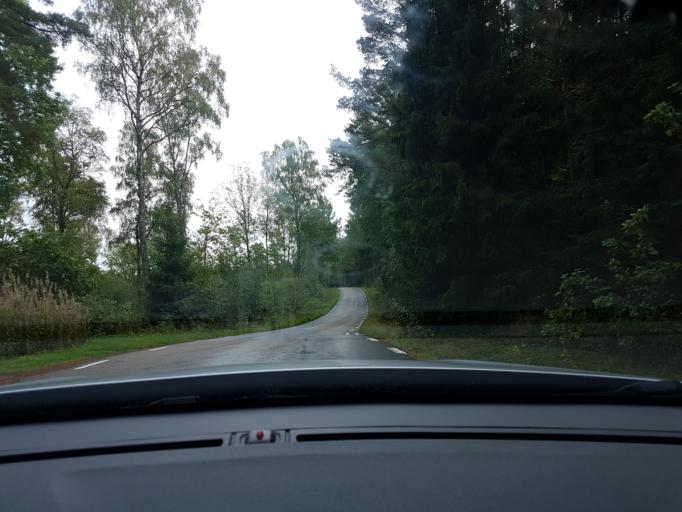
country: SE
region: Vaestra Goetaland
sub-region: Ale Kommun
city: Alvangen
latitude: 57.9019
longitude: 12.1820
